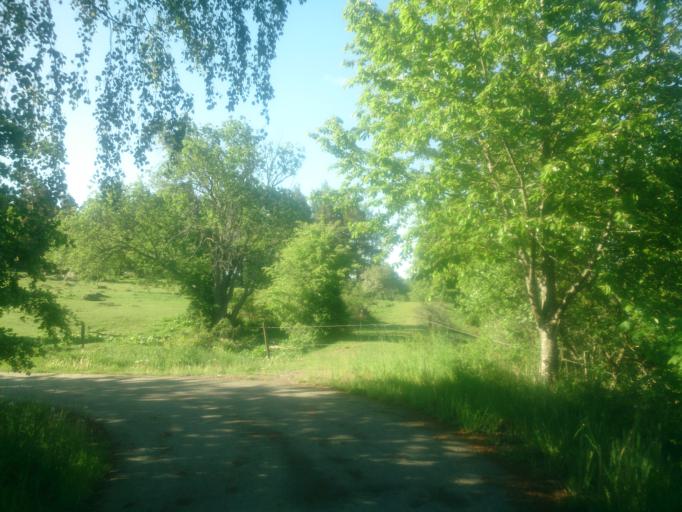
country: SE
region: OEstergoetland
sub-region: Atvidabergs Kommun
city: Atvidaberg
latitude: 58.2194
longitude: 15.9785
